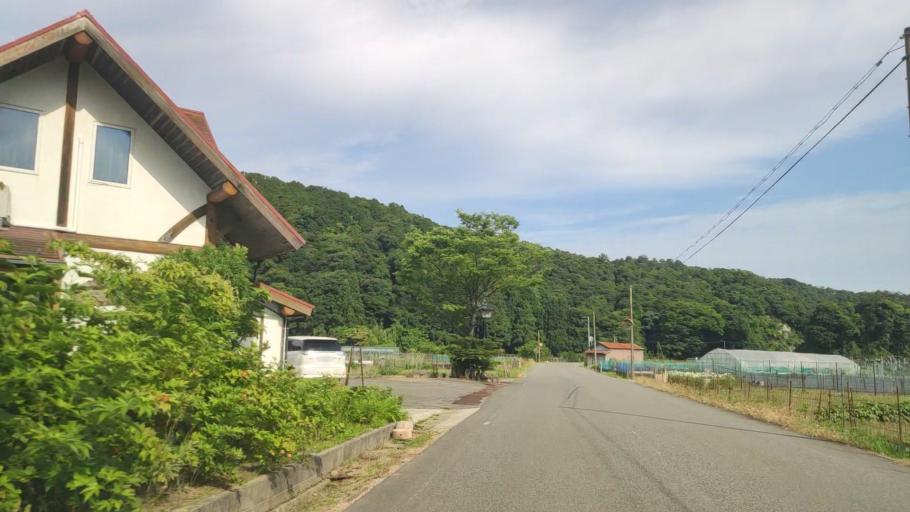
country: JP
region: Hyogo
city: Toyooka
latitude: 35.6337
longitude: 134.8384
